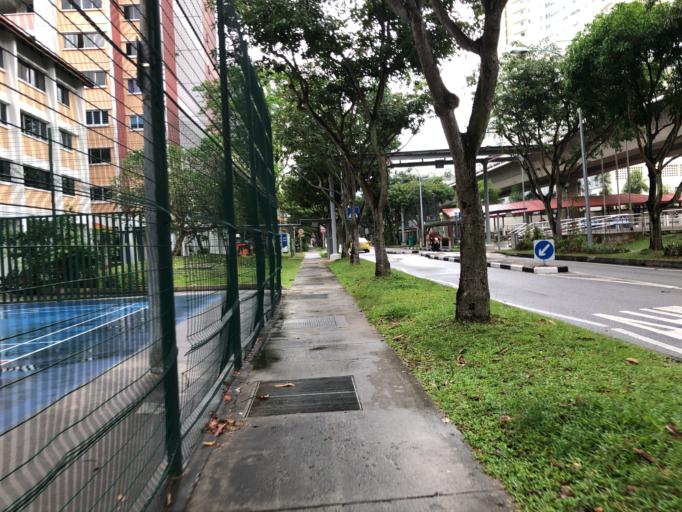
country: MY
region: Johor
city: Johor Bahru
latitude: 1.3537
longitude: 103.7522
